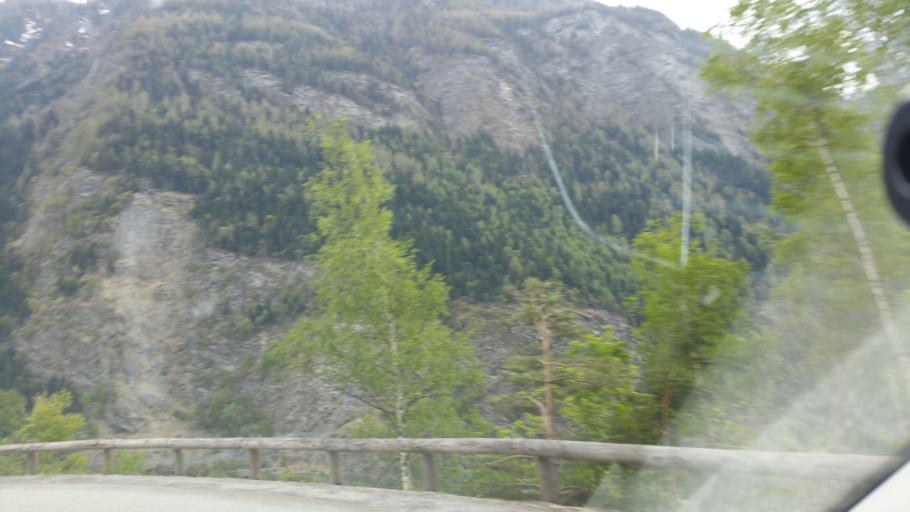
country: FR
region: Rhone-Alpes
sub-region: Departement de la Savoie
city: Modane
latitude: 45.2039
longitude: 6.6025
